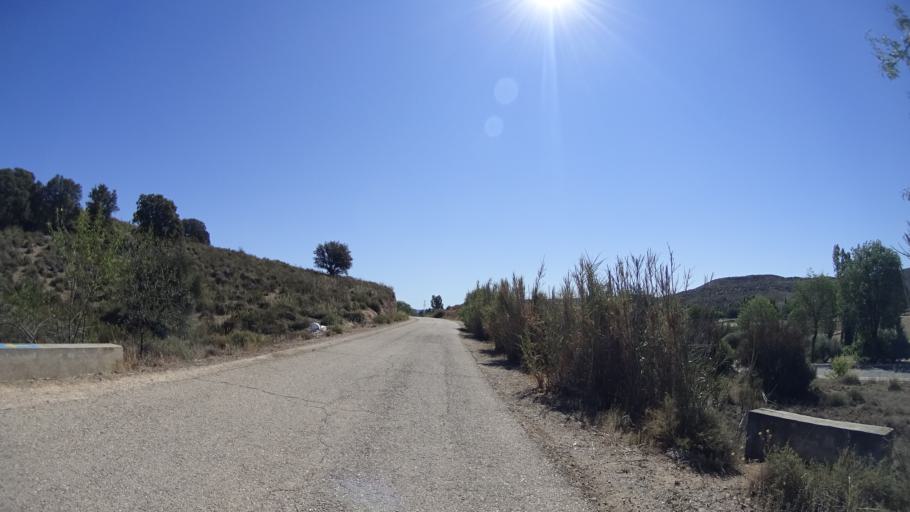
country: ES
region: Madrid
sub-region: Provincia de Madrid
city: Morata de Tajuna
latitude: 40.2296
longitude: -3.4192
